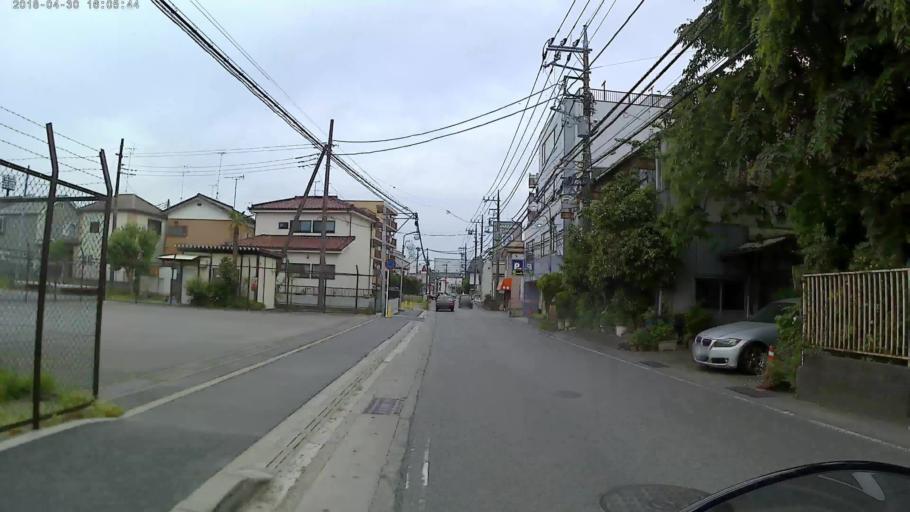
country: JP
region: Kanagawa
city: Minami-rinkan
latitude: 35.5033
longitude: 139.4276
